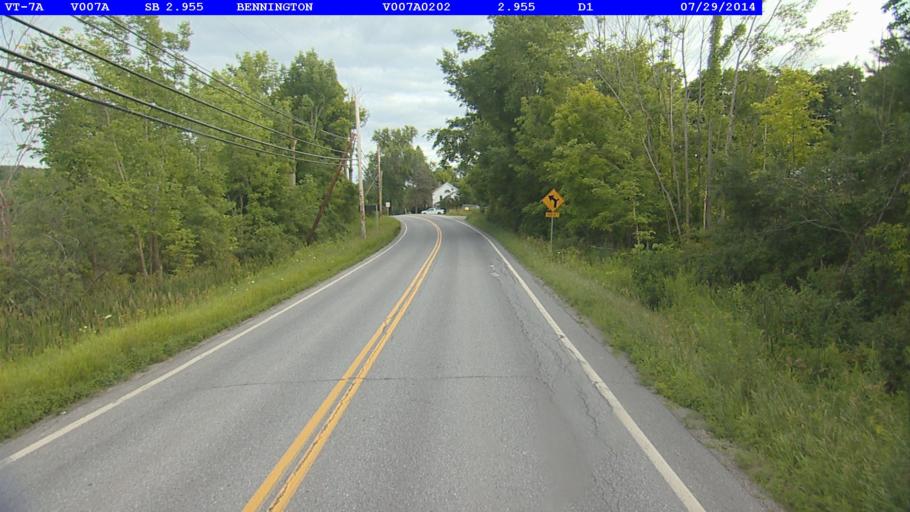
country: US
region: Vermont
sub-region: Bennington County
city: North Bennington
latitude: 42.9317
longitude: -73.2101
